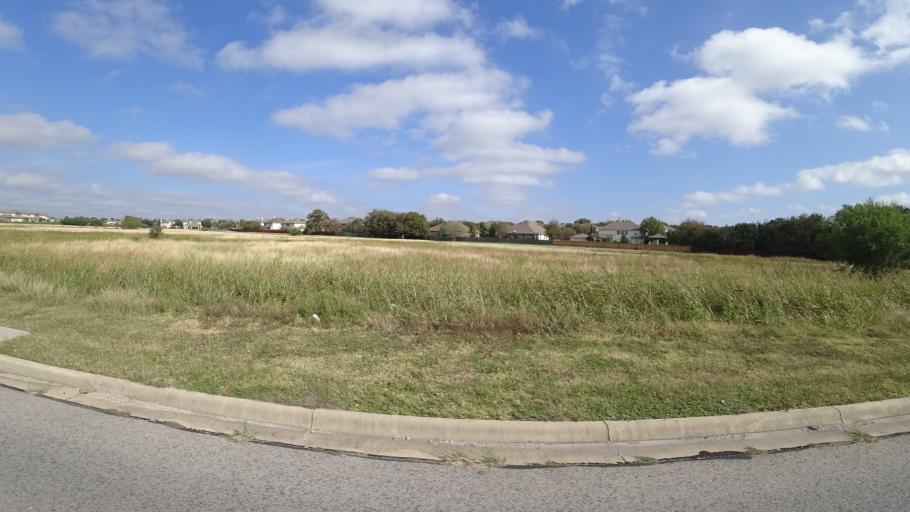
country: US
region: Texas
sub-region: Travis County
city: Pflugerville
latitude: 30.4279
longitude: -97.6322
